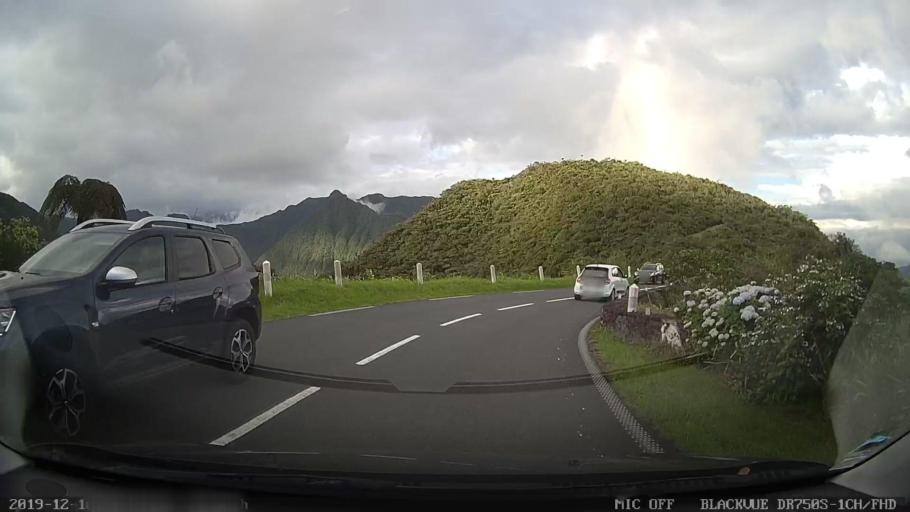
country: RE
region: Reunion
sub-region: Reunion
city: Cilaos
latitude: -21.1579
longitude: 55.5966
